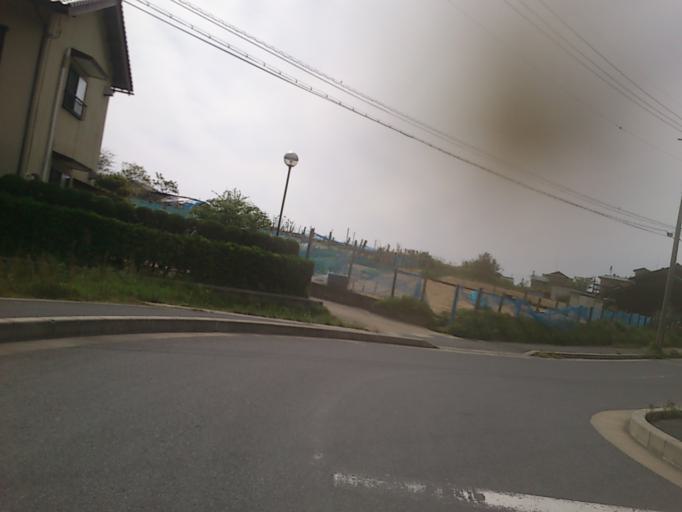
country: JP
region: Hyogo
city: Toyooka
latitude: 35.6674
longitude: 134.9711
